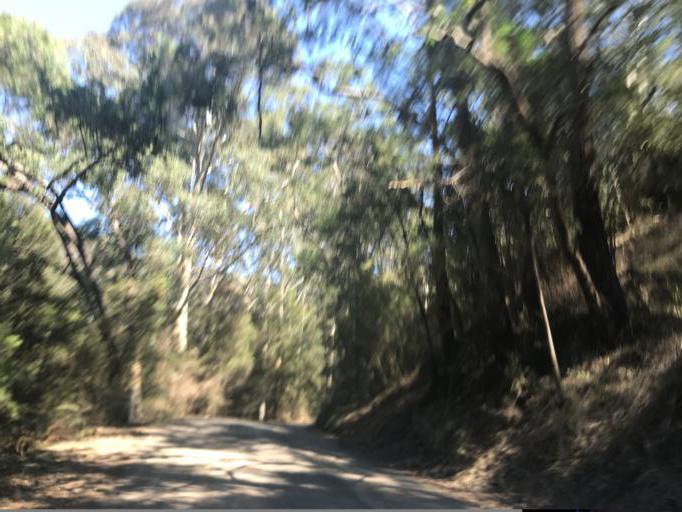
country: AU
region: New South Wales
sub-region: Wyong Shire
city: Little Jilliby
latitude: -33.1960
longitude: 151.0204
